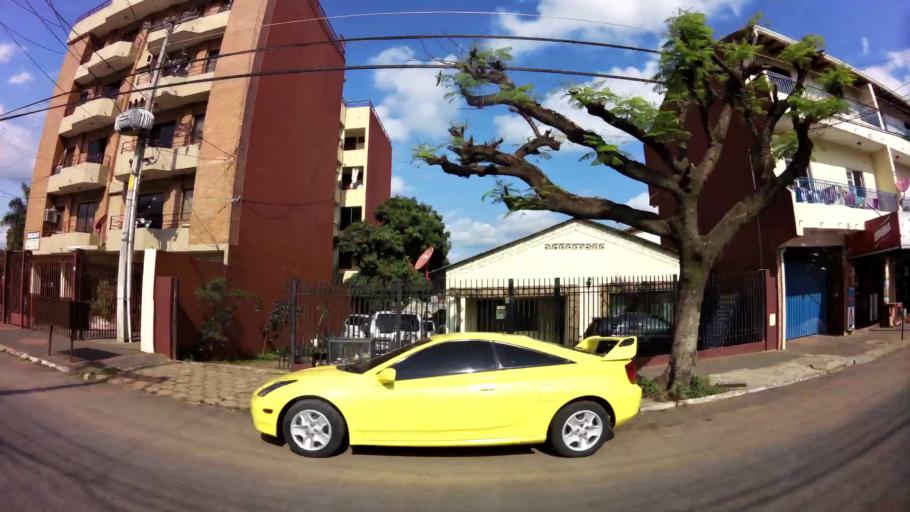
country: PY
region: Central
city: Fernando de la Mora
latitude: -25.3338
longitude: -57.5317
